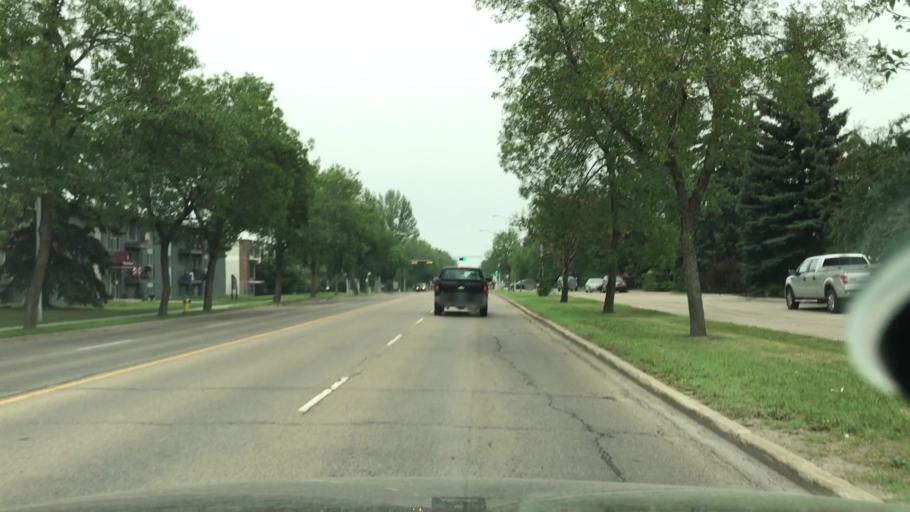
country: CA
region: Alberta
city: Edmonton
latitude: 53.5235
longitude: -113.5779
